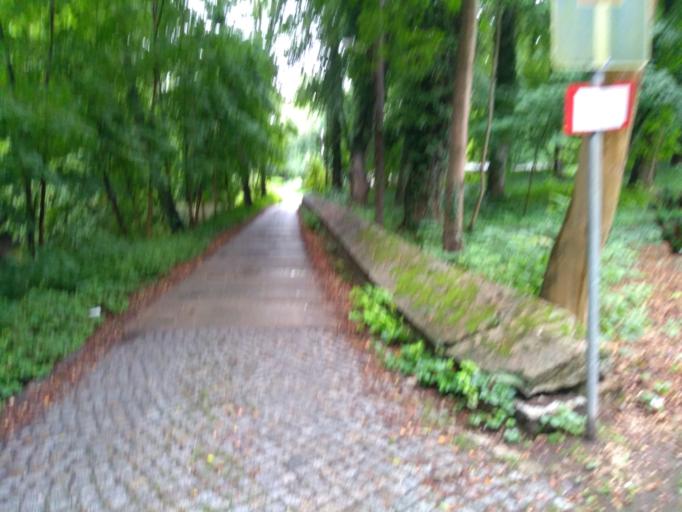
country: DE
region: Saxony
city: Bautzen
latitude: 51.1767
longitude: 14.4183
